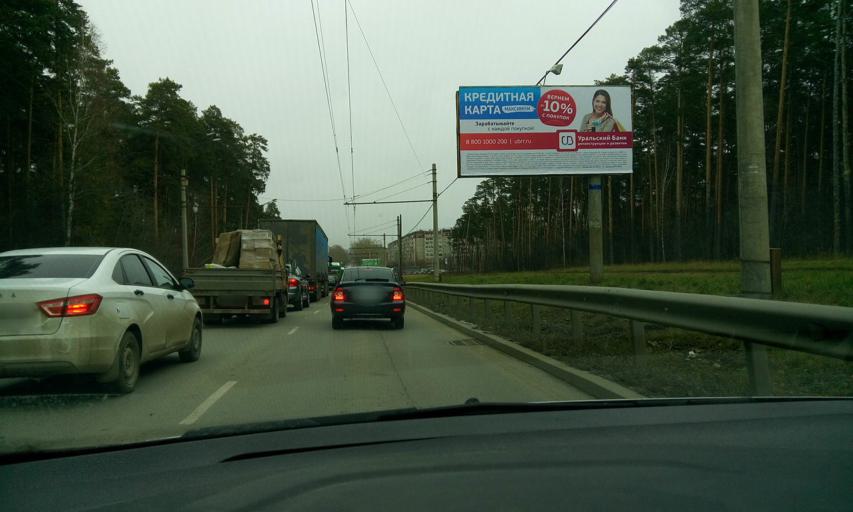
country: RU
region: Sverdlovsk
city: Sovkhoznyy
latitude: 56.7890
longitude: 60.5699
